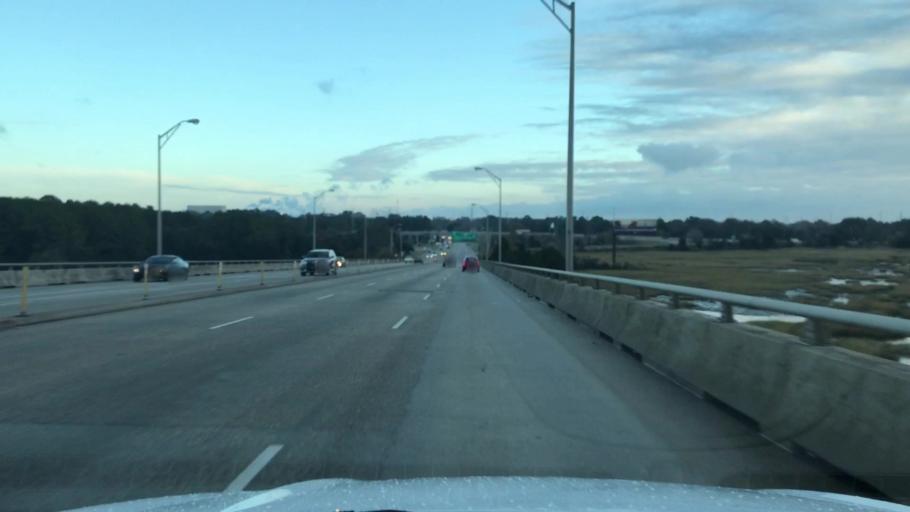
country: US
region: South Carolina
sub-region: Charleston County
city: North Charleston
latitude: 32.8385
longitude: -79.9836
